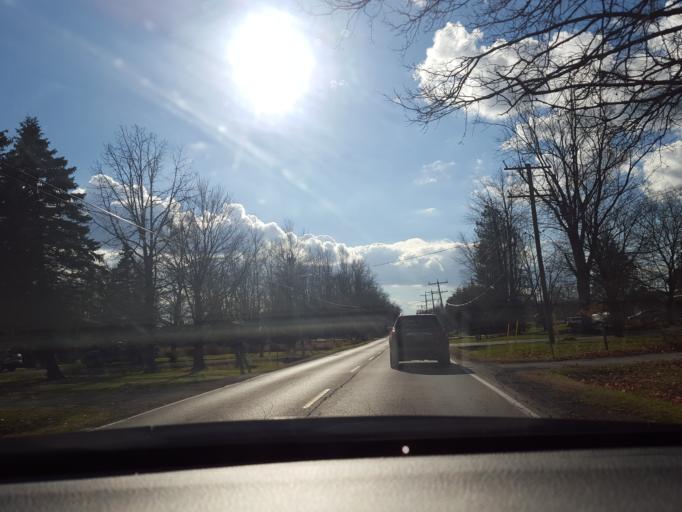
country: CA
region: Ontario
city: Burlington
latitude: 43.3834
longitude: -79.9959
